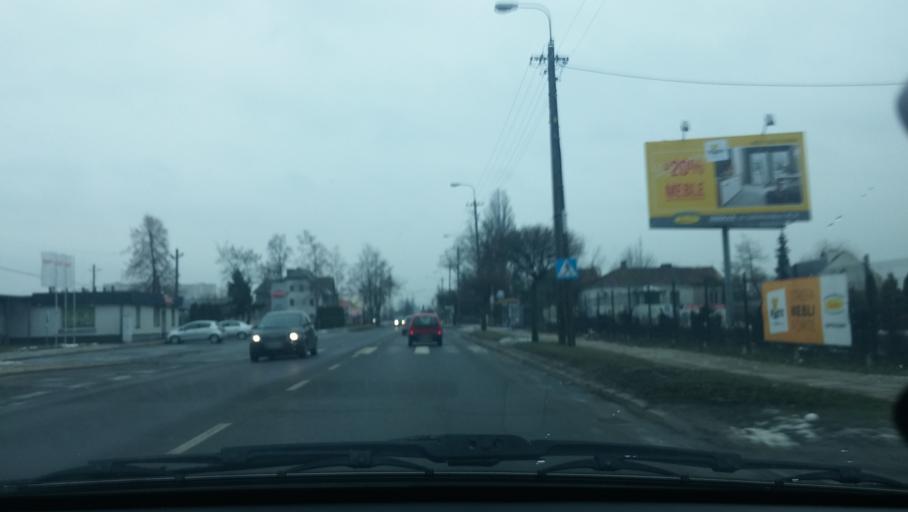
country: PL
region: Masovian Voivodeship
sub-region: Siedlce
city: Siedlce
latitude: 52.1871
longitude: 22.2672
